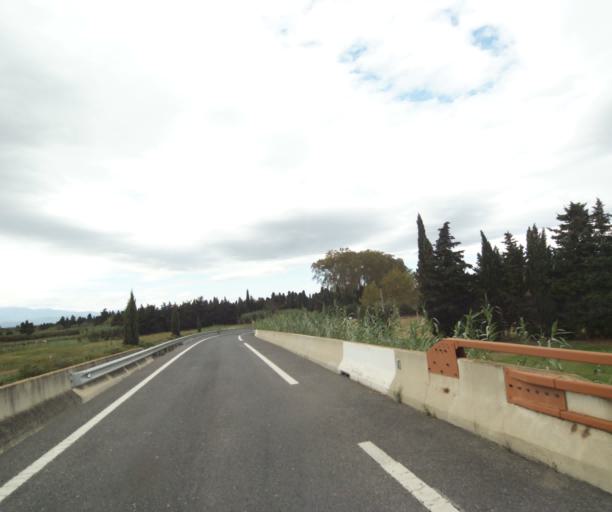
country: FR
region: Languedoc-Roussillon
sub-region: Departement des Pyrenees-Orientales
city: Elne
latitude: 42.5897
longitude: 2.9820
